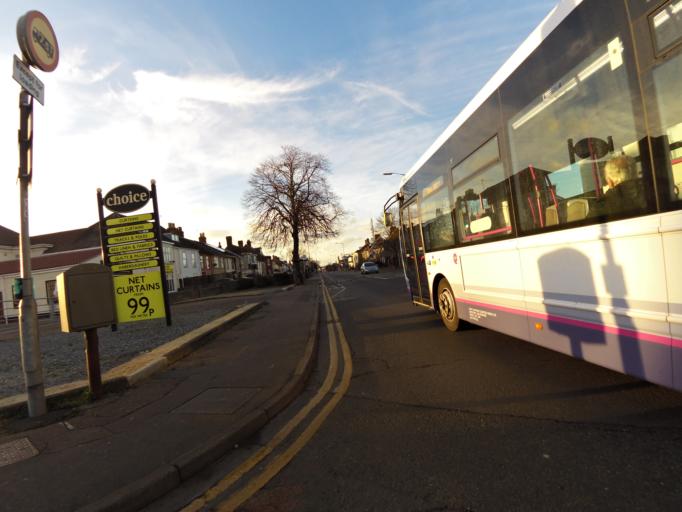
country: GB
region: England
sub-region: Norfolk
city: Great Yarmouth
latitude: 52.5998
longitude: 1.7237
